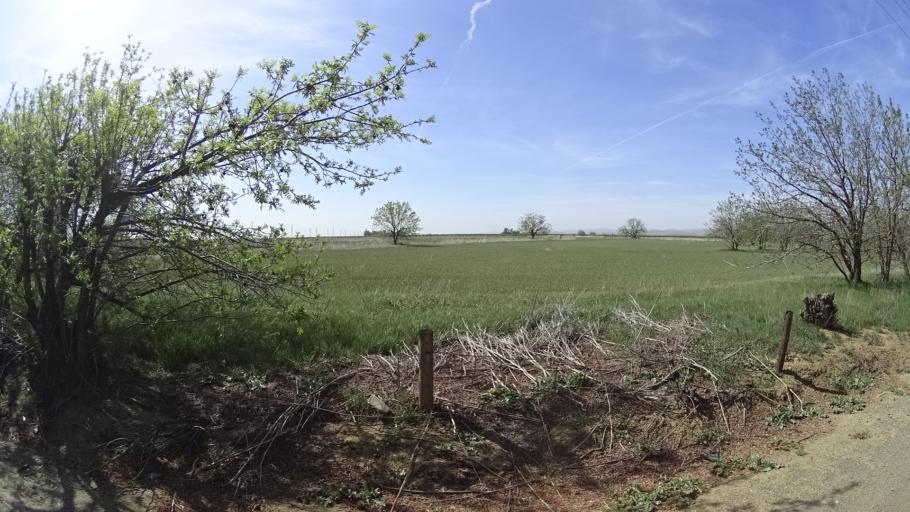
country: US
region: California
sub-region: Glenn County
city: Willows
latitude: 39.5388
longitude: -122.2673
